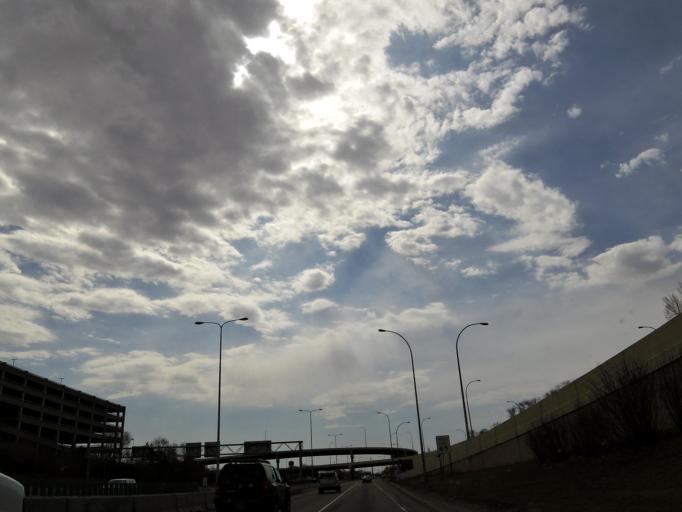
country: US
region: Minnesota
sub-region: Hennepin County
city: Richfield
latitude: 44.8550
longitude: -93.2473
